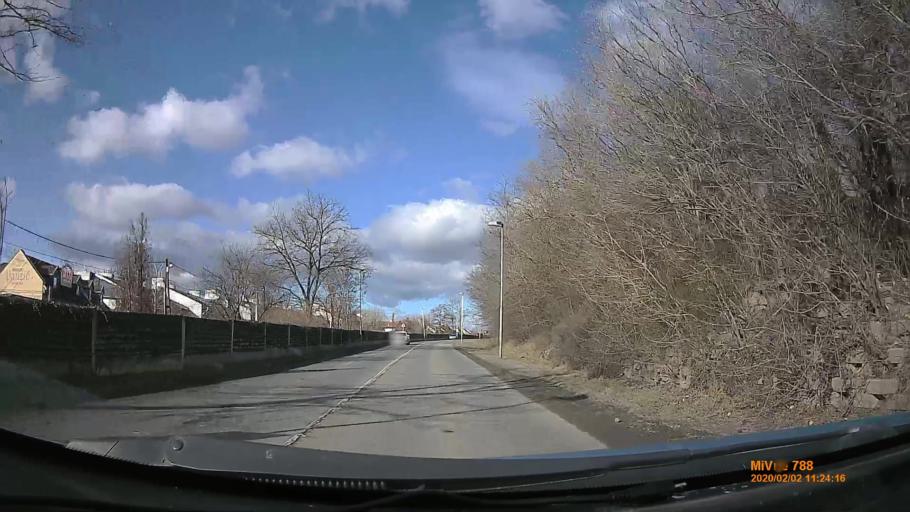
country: HU
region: Gyor-Moson-Sopron
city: Sopron
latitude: 47.6946
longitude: 16.5857
